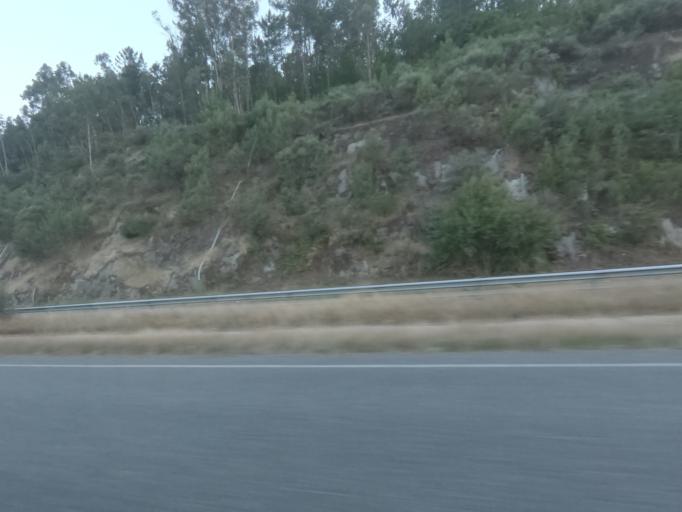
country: ES
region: Galicia
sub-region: Provincia de Pontevedra
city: Ponteareas
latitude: 42.1757
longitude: -8.5582
